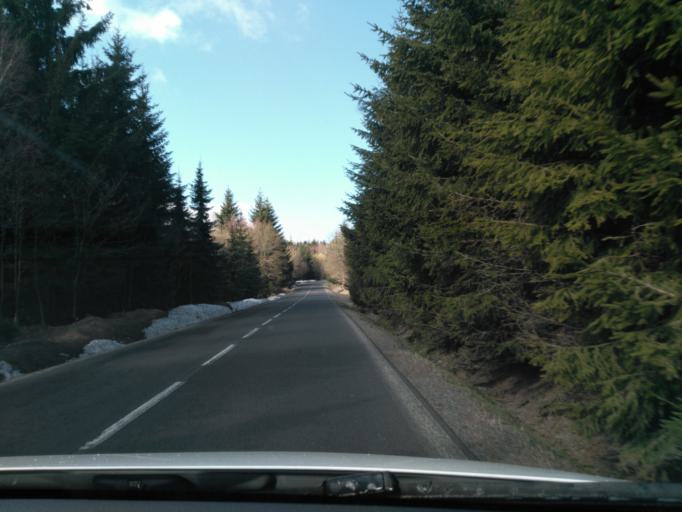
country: CZ
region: Ustecky
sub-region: Okres Chomutov
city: Kovarska
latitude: 50.4590
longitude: 13.0466
